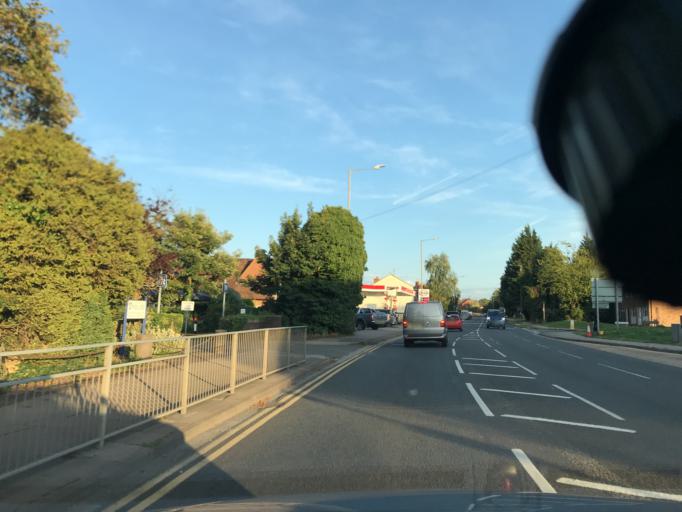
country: GB
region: England
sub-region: Buckinghamshire
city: Aylesbury
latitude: 51.8105
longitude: -0.8048
